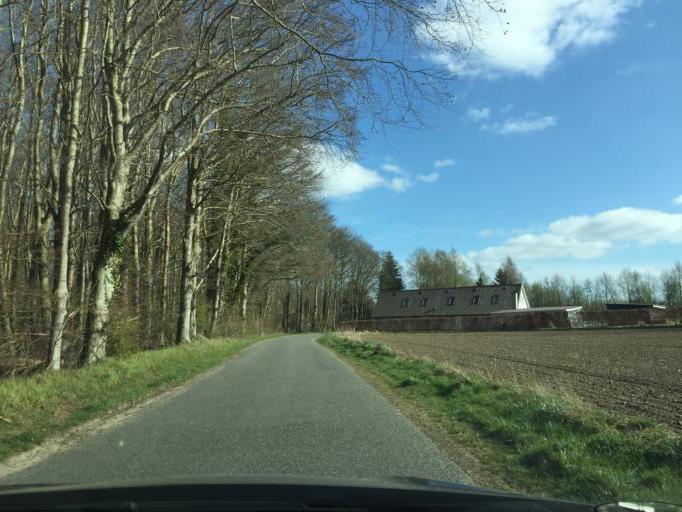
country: DK
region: South Denmark
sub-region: Faaborg-Midtfyn Kommune
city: Arslev
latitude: 55.2987
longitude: 10.4979
